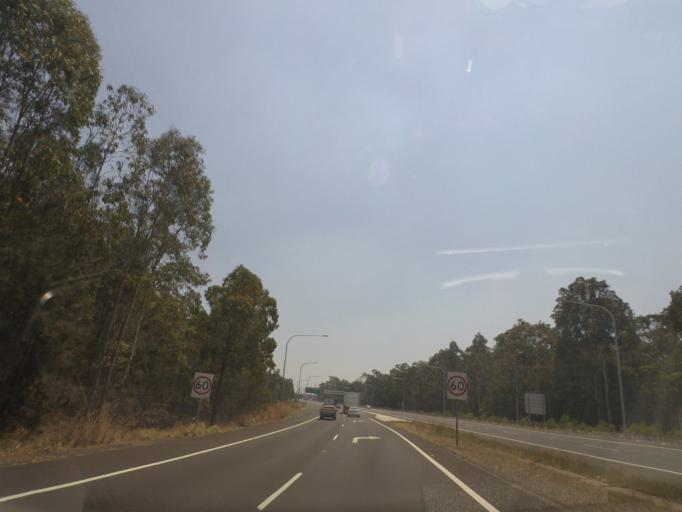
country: AU
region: New South Wales
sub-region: Newcastle
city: Beresfield
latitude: -32.8178
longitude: 151.6354
